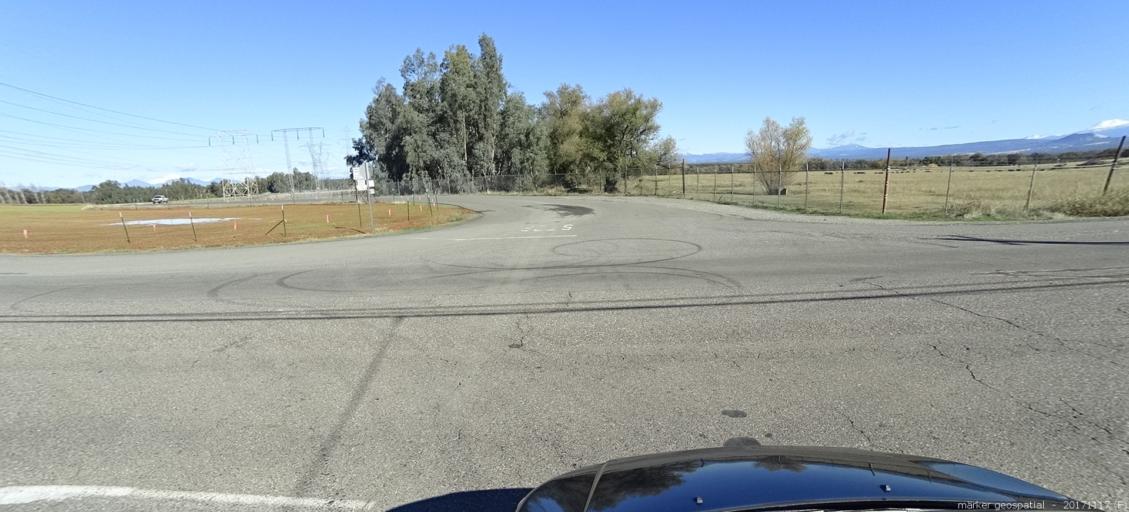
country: US
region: California
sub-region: Shasta County
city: Anderson
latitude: 40.4334
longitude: -122.2357
